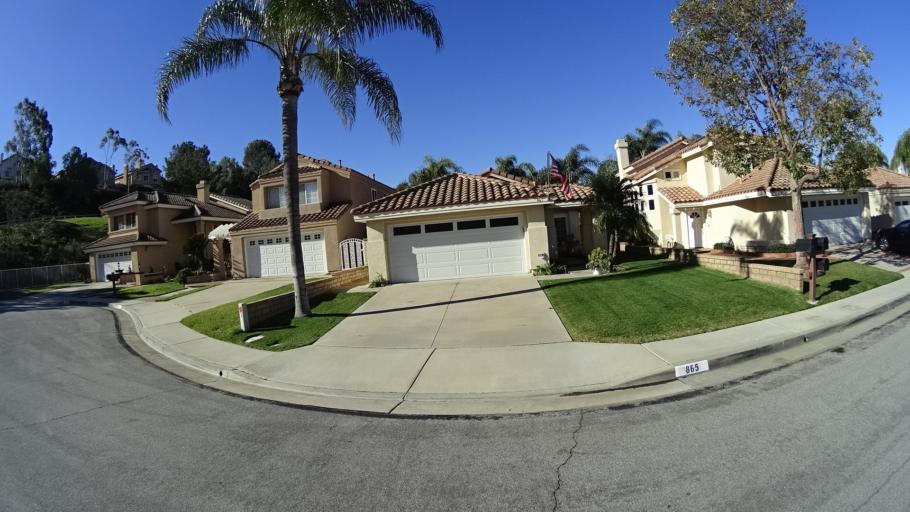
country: US
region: California
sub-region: Orange County
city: Yorba Linda
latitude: 33.8590
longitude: -117.7354
